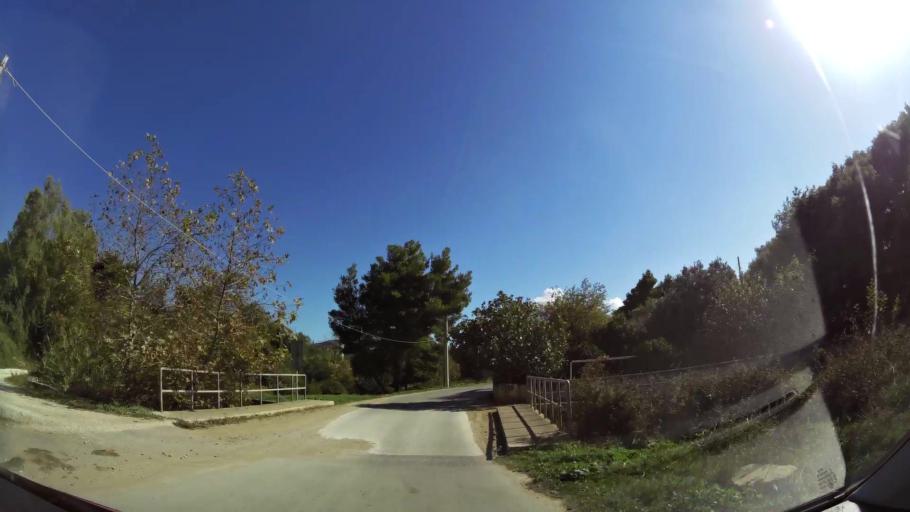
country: GR
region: Attica
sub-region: Nomarchia Anatolikis Attikis
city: Pikermi
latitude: 38.0073
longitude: 23.9413
